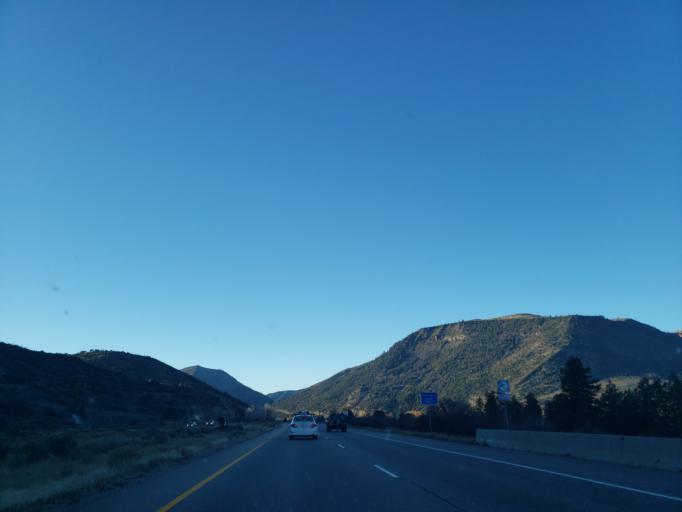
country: US
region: Colorado
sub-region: Pitkin County
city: Snowmass Village
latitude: 39.2796
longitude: -106.8979
